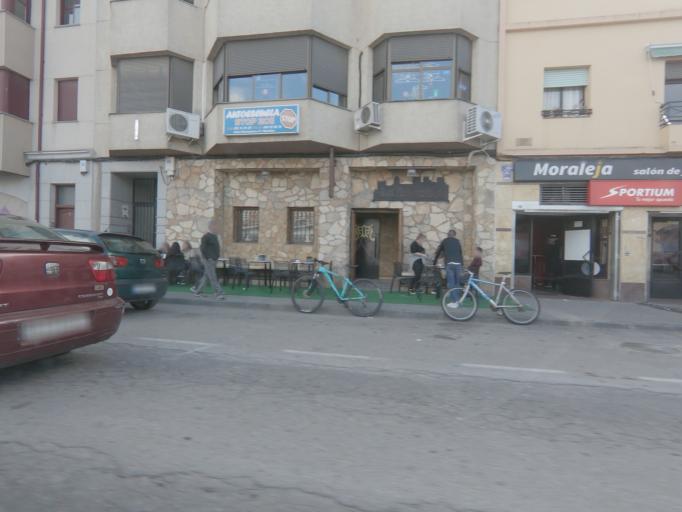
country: ES
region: Extremadura
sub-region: Provincia de Caceres
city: Moraleja
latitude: 40.0707
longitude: -6.6579
